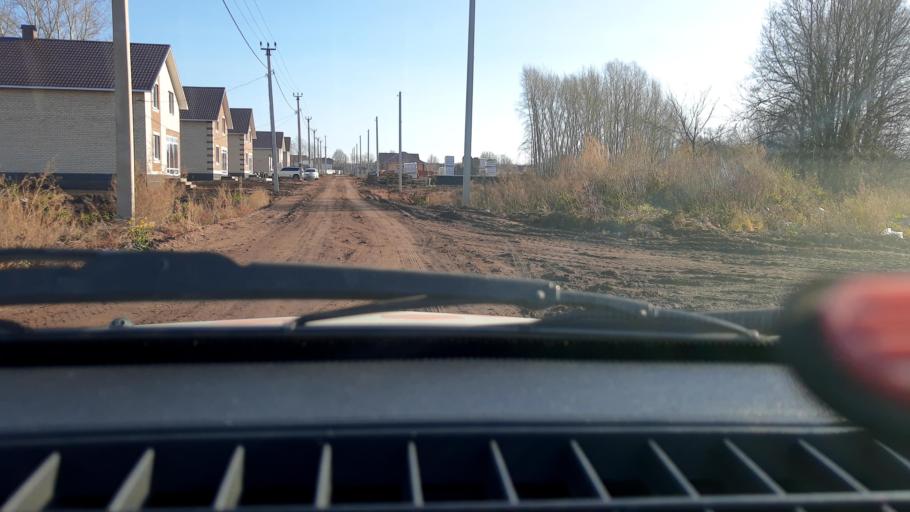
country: RU
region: Bashkortostan
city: Kabakovo
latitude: 54.6275
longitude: 56.1293
